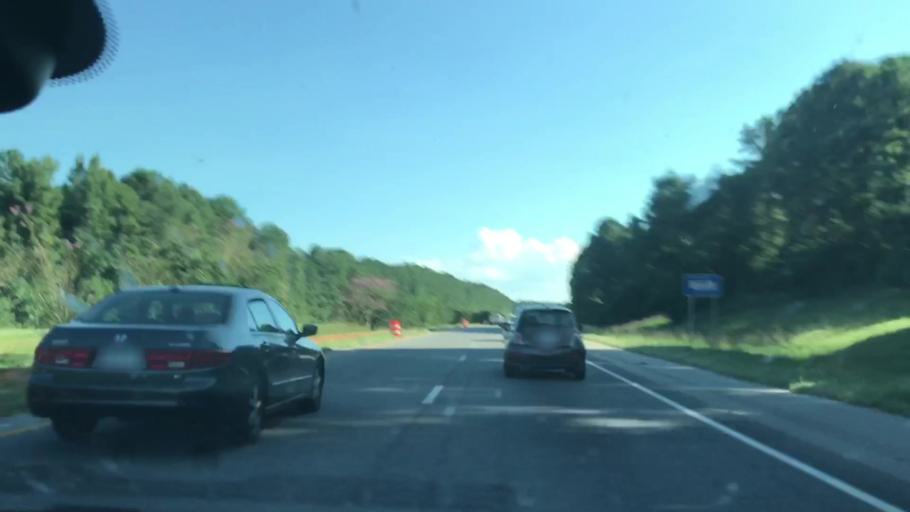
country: US
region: Georgia
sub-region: Harris County
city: Hamilton
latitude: 32.7835
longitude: -85.0203
